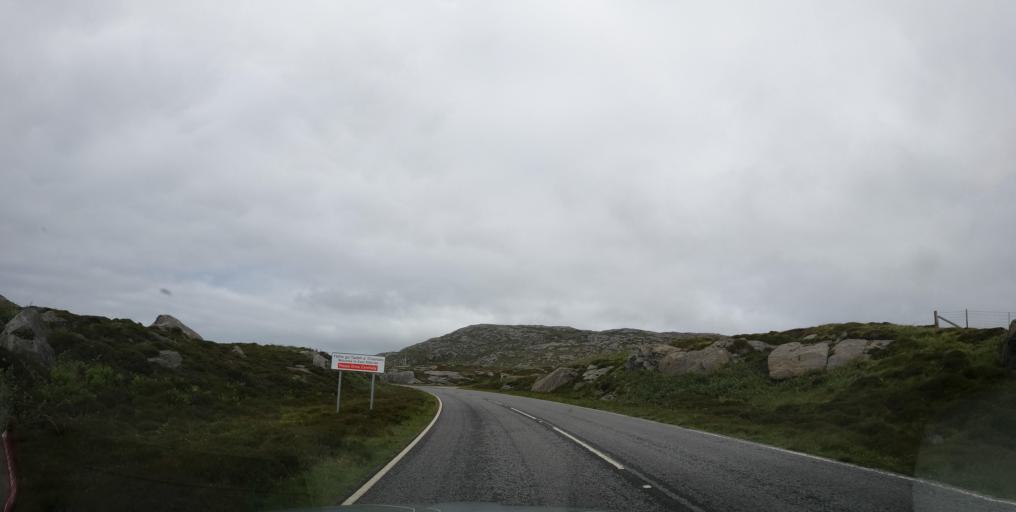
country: GB
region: Scotland
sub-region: Eilean Siar
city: Isle of South Uist
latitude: 57.1051
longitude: -7.3193
